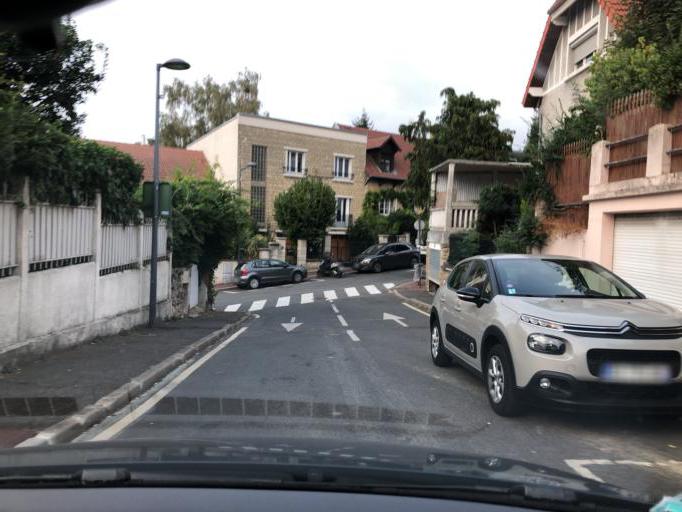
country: FR
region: Ile-de-France
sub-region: Departement des Hauts-de-Seine
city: Ville-d'Avray
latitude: 48.8164
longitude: 2.1972
